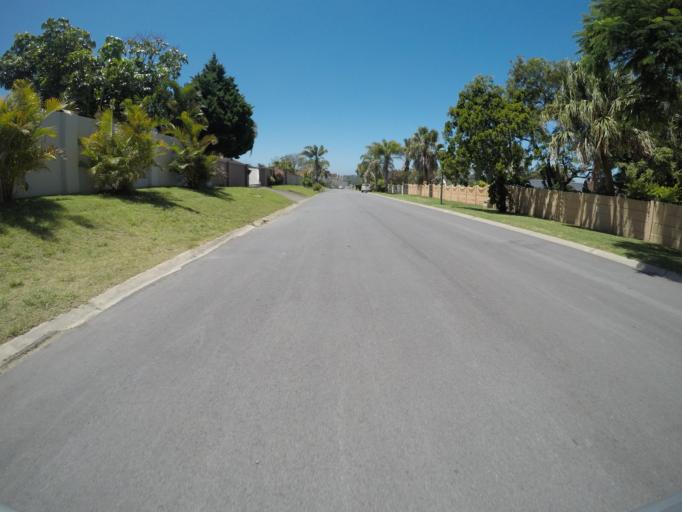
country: ZA
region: Eastern Cape
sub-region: Buffalo City Metropolitan Municipality
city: East London
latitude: -32.9547
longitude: 27.9375
